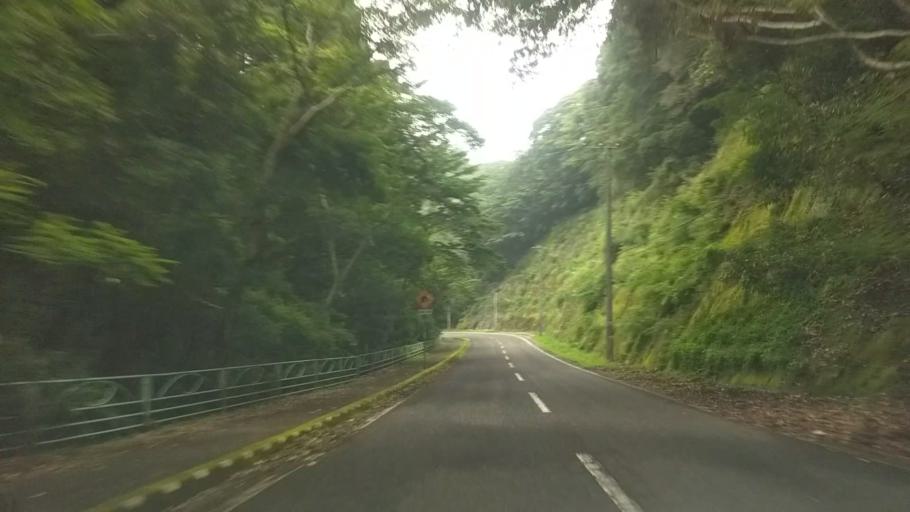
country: JP
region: Chiba
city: Kawaguchi
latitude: 35.1621
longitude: 140.1413
